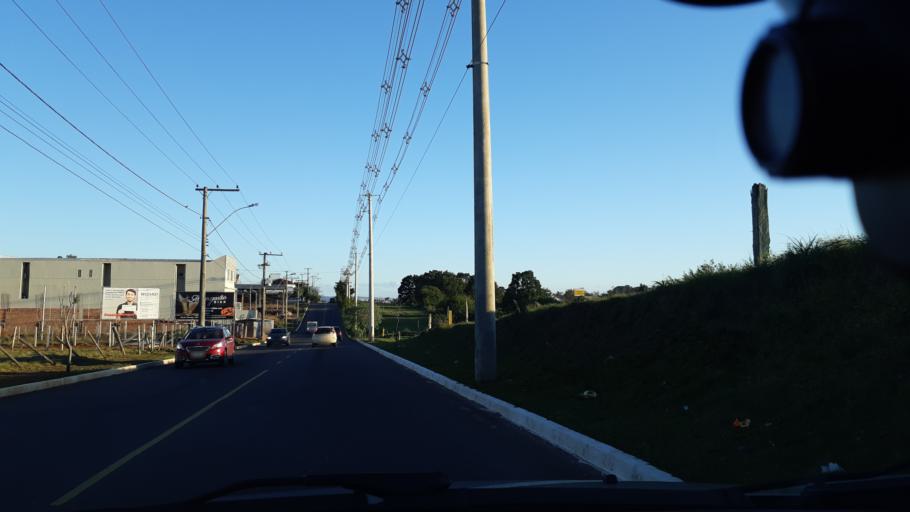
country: BR
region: Rio Grande do Sul
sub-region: Canoas
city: Canoas
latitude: -29.9125
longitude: -51.1540
